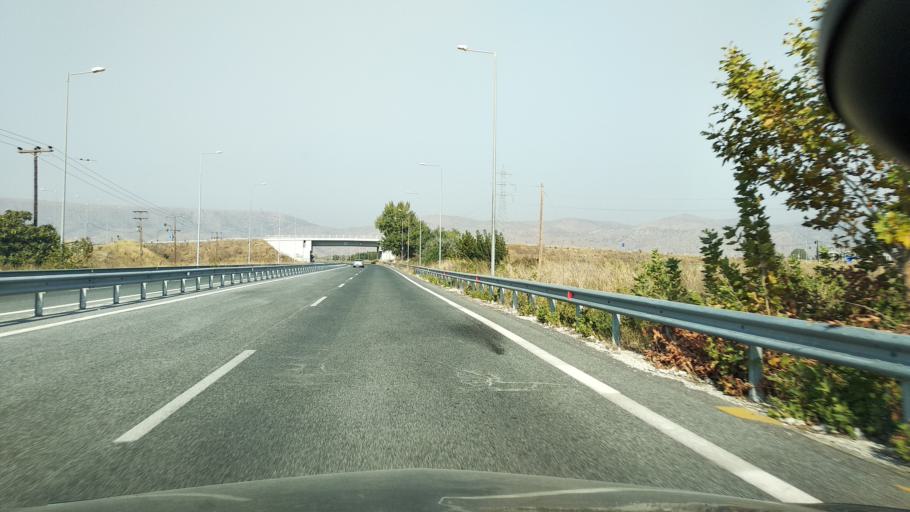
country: GR
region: Thessaly
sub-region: Trikala
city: Zarkos
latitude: 39.5923
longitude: 22.1261
